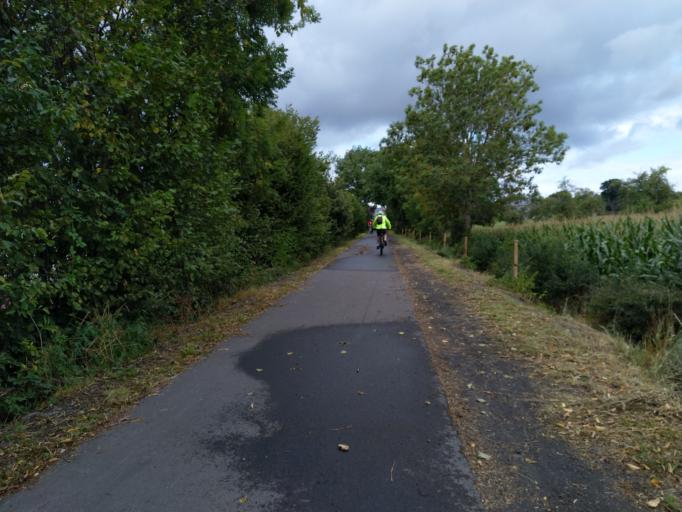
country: BE
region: Wallonia
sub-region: Province de Liege
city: Aubel
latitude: 50.6953
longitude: 5.8559
